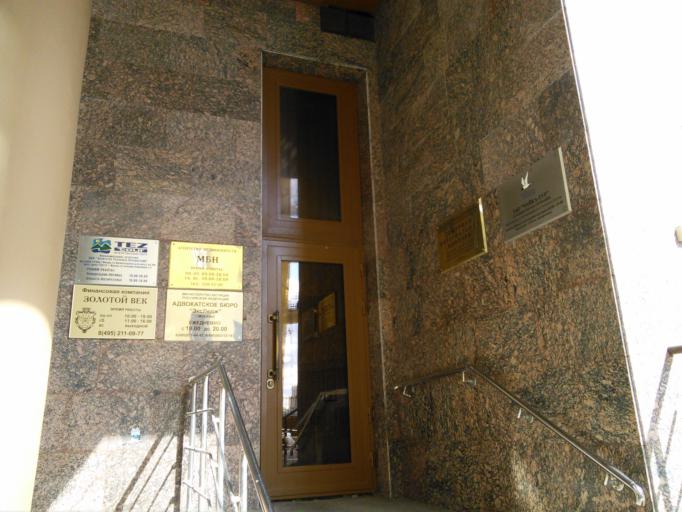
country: RU
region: Moscow
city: Taganskiy
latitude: 55.7391
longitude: 37.6525
